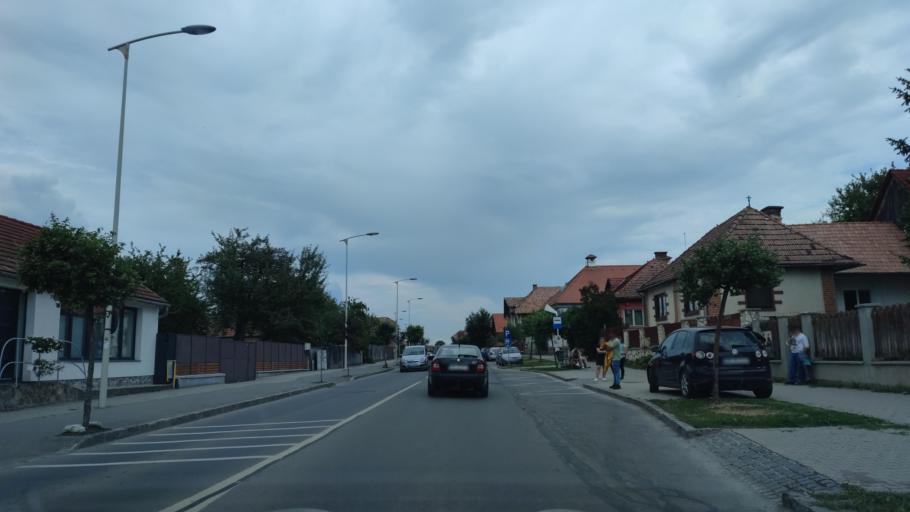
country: RO
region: Harghita
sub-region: Municipiul Miercurea Ciuc
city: Miercurea-Ciuc
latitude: 46.3705
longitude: 25.8049
